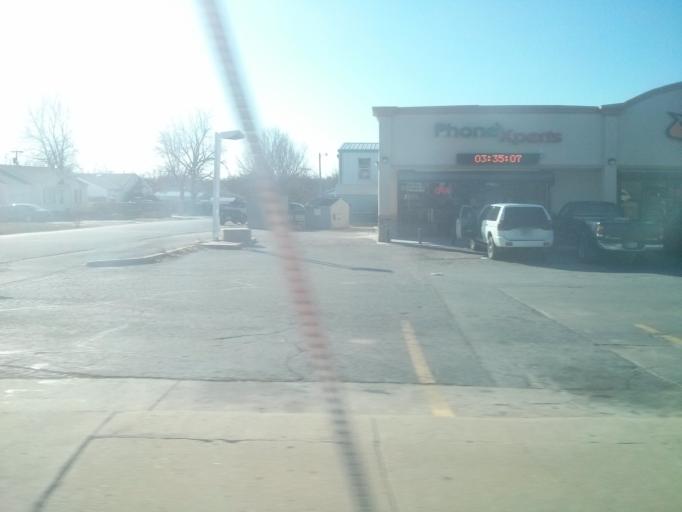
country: US
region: Oklahoma
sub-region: Tulsa County
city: Tulsa
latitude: 36.1769
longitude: -95.9399
